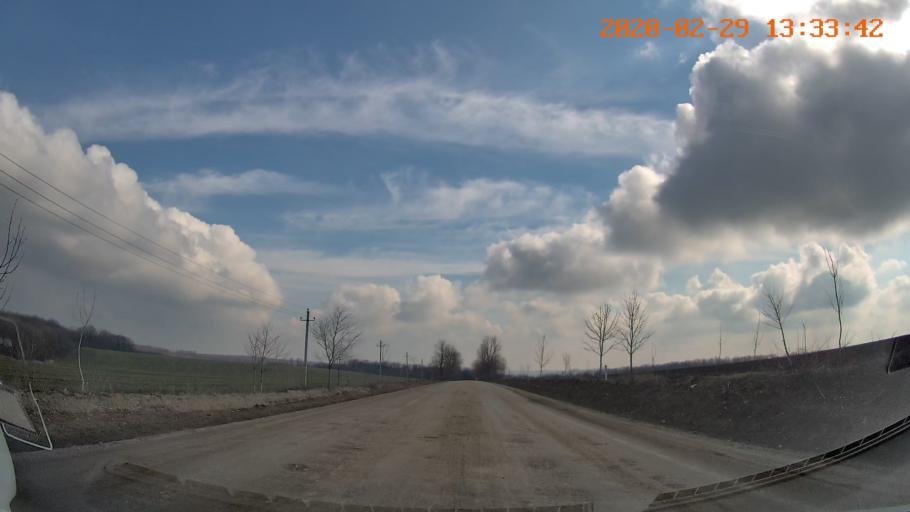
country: MD
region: Telenesti
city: Camenca
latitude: 47.8722
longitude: 28.6182
